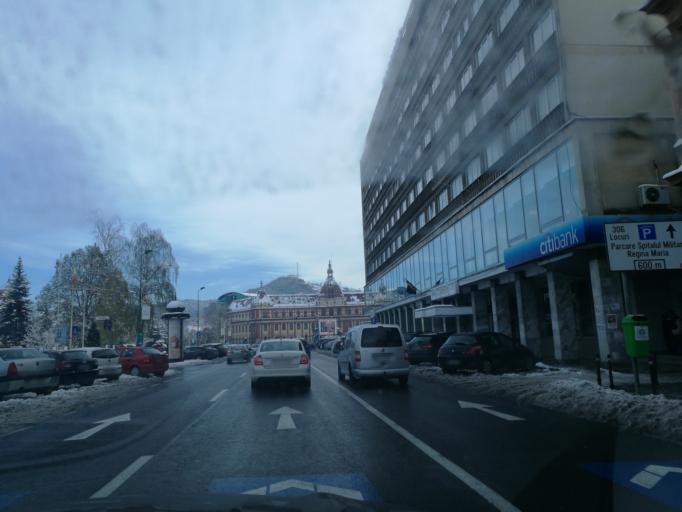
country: RO
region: Brasov
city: Brasov
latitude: 45.6452
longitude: 25.5936
